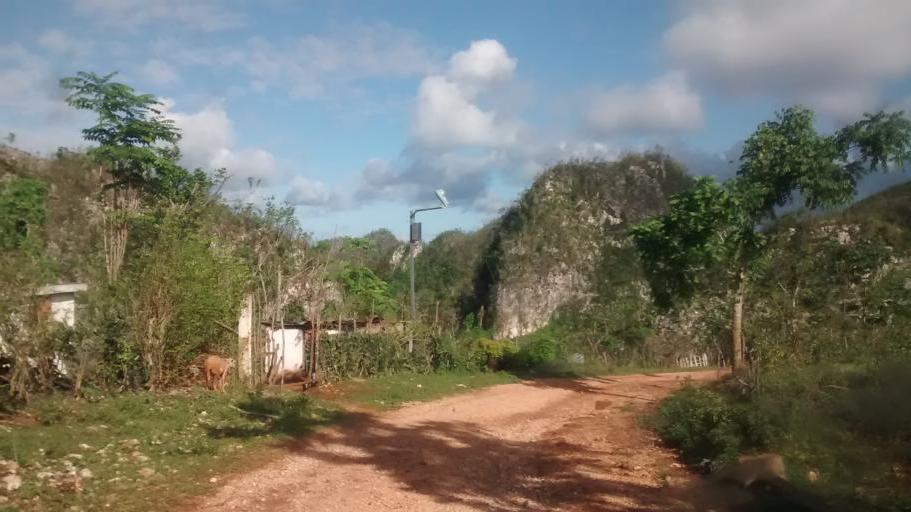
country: HT
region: Grandans
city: Corail
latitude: 18.5312
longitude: -73.8468
